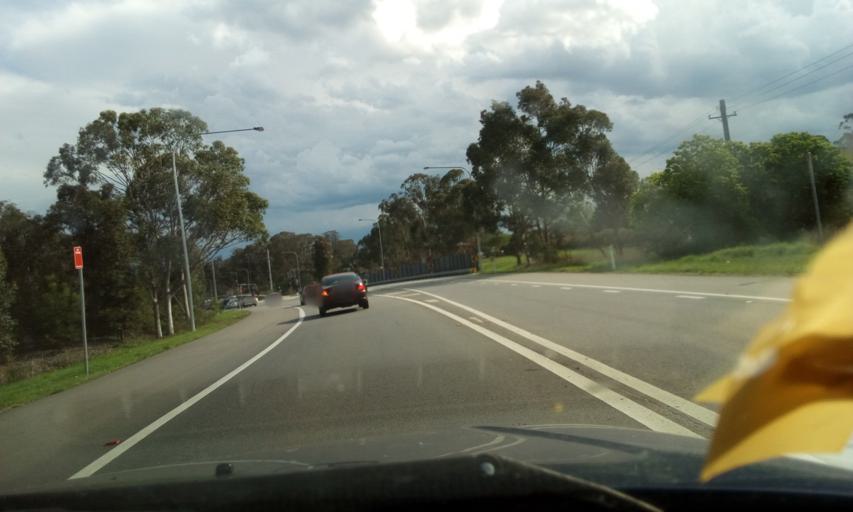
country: AU
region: New South Wales
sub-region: Penrith Municipality
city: Werrington Downs
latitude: -33.7206
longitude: 150.7238
